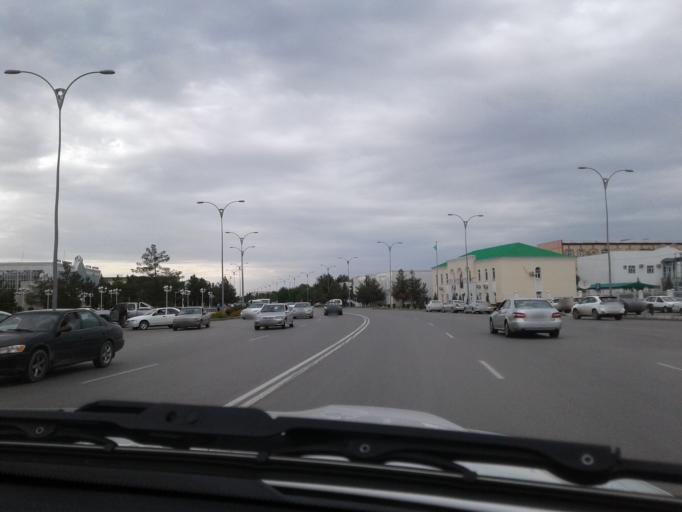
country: TM
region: Mary
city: Mary
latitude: 37.5885
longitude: 61.8398
